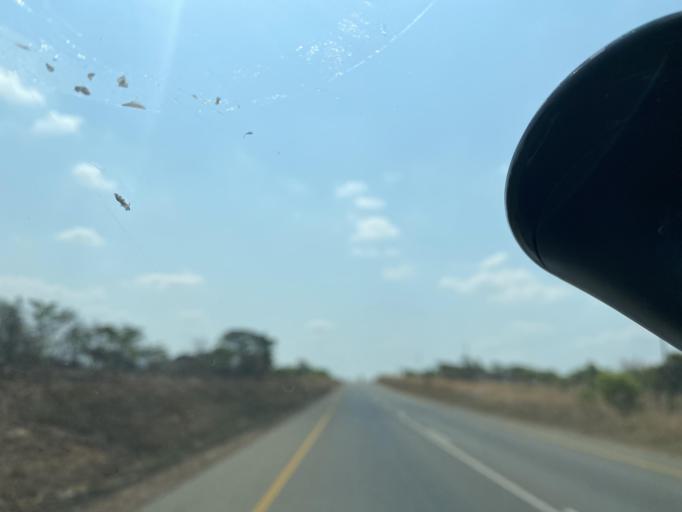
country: ZM
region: Lusaka
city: Chongwe
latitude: -15.5386
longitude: 28.6549
